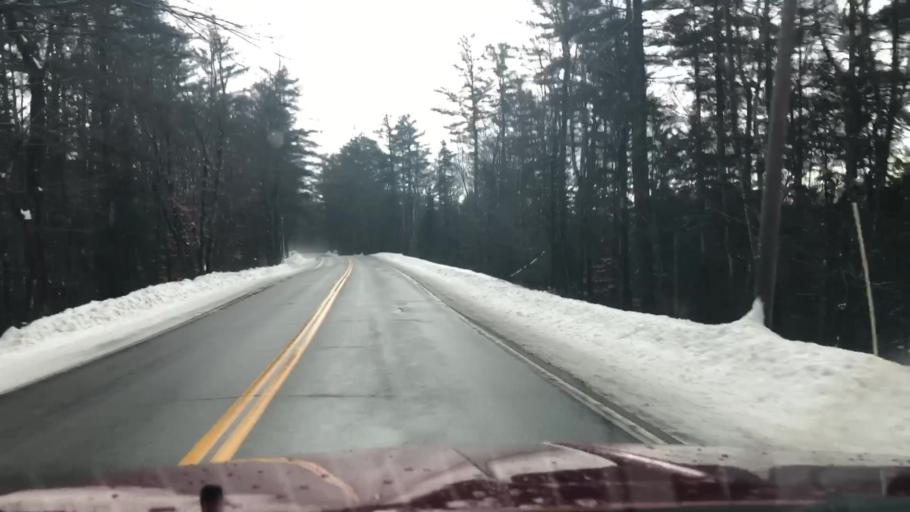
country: US
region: Maine
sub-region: Oxford County
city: West Paris
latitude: 44.4148
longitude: -70.6442
